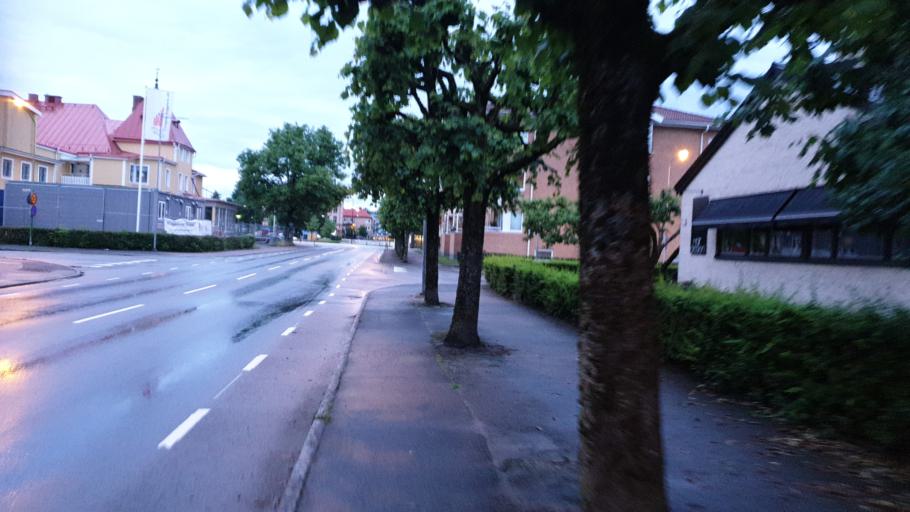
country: SE
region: Kronoberg
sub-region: Ljungby Kommun
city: Ljungby
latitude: 56.8307
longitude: 13.9398
